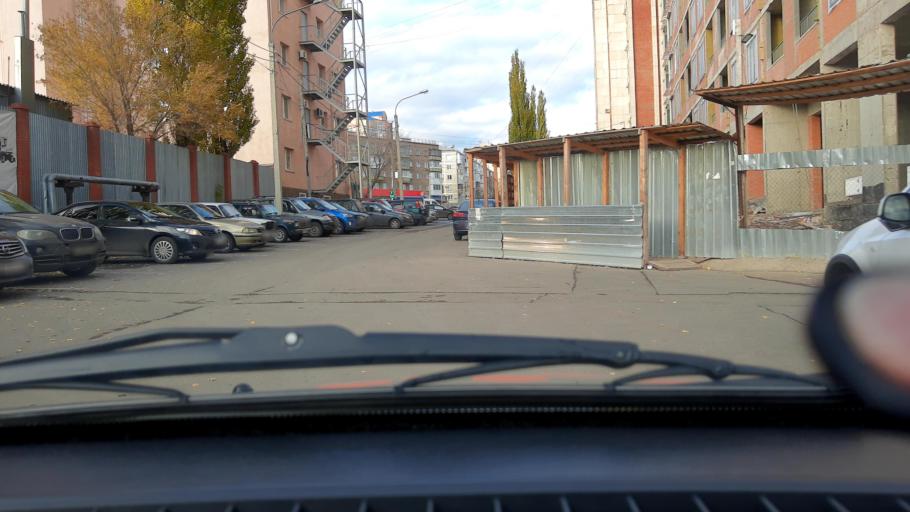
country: RU
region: Bashkortostan
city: Ufa
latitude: 54.7252
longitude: 55.9817
